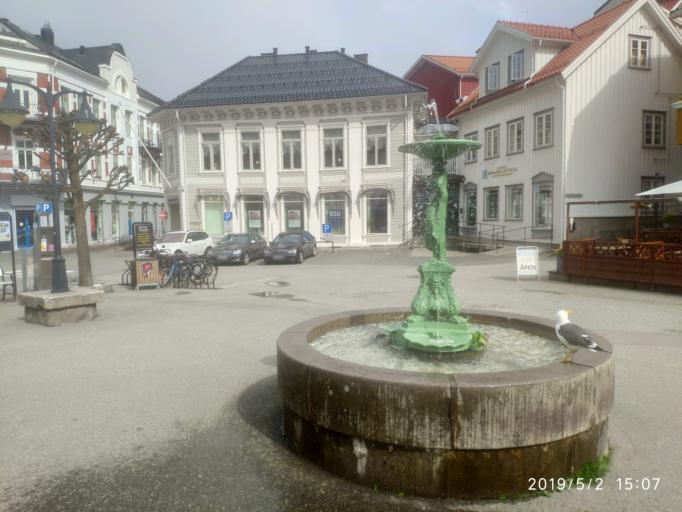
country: NO
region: Telemark
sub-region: Kragero
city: Kragero
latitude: 58.8692
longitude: 9.4114
